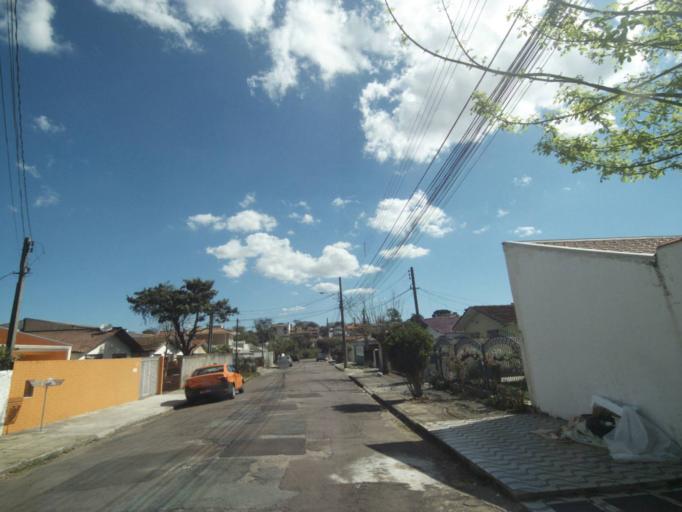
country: BR
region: Parana
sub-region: Curitiba
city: Curitiba
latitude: -25.3806
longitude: -49.2479
